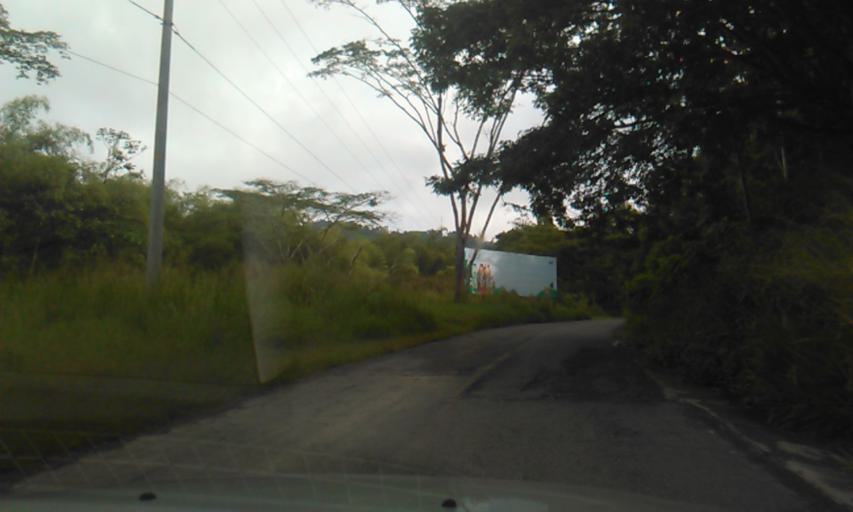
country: CO
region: Quindio
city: Cordoba
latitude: 4.4074
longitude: -75.7043
